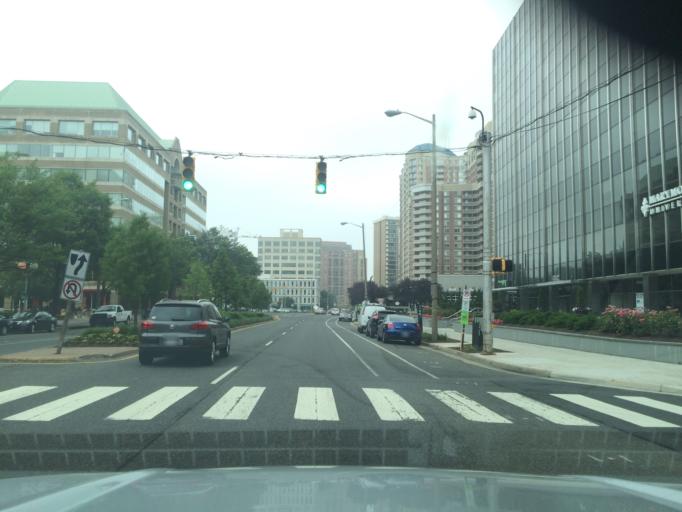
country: US
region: Virginia
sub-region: Arlington County
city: Arlington
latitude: 38.8824
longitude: -77.1095
